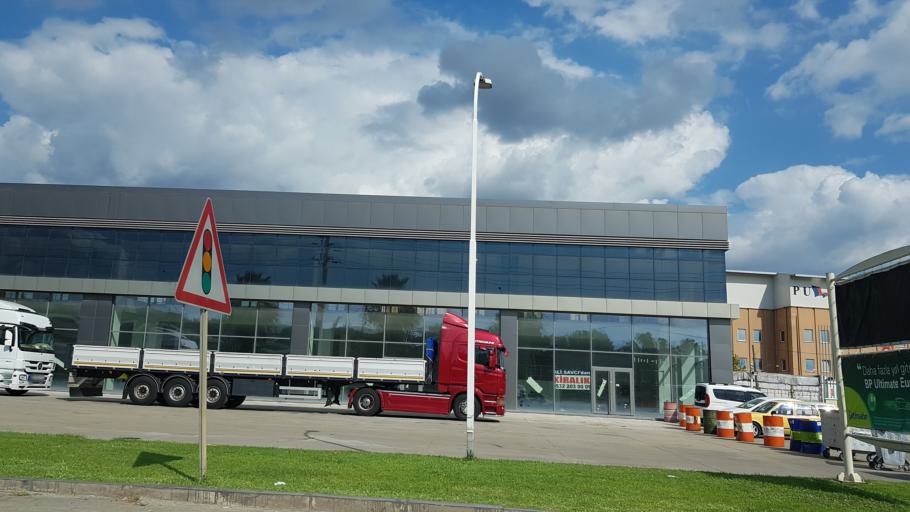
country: TR
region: Bursa
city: Demirtas
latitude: 40.2814
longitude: 29.0532
